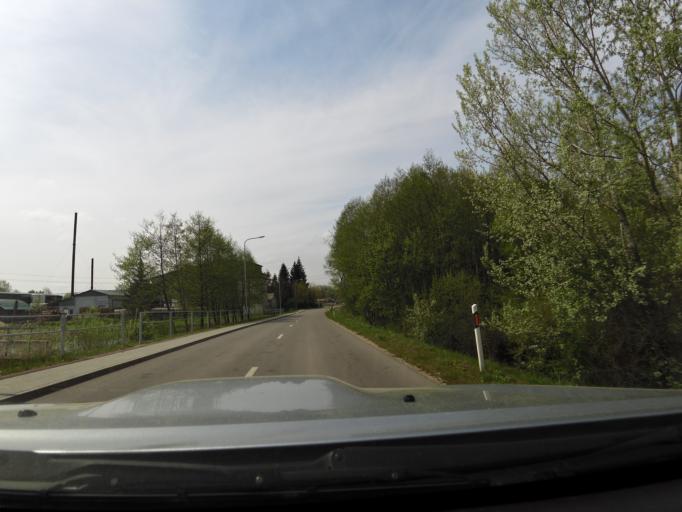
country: LT
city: Salcininkai
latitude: 54.4321
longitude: 25.3080
